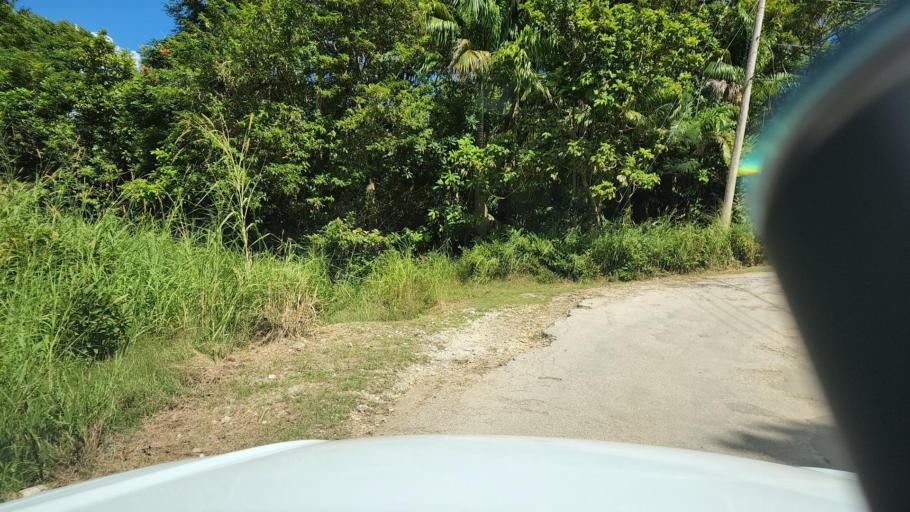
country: BB
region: Saint Thomas
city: Welchman Hall
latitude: 13.1936
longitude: -59.5536
